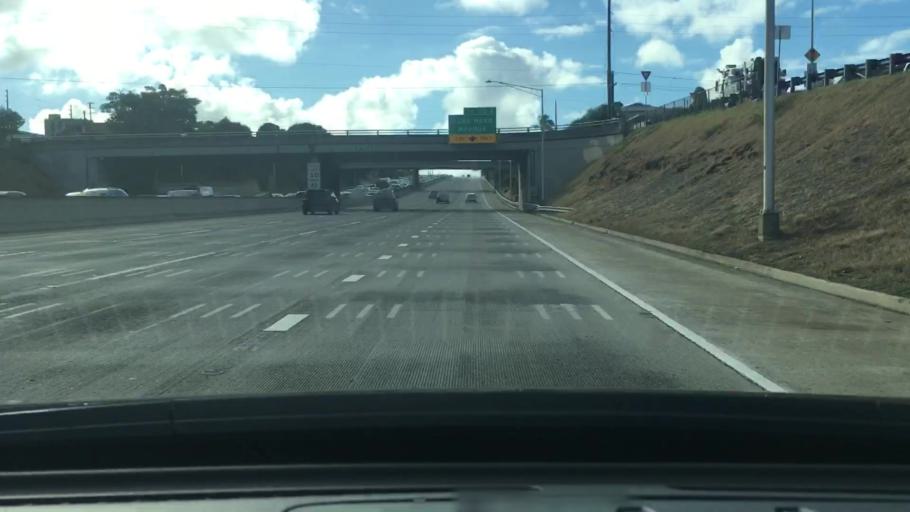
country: US
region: Hawaii
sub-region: Honolulu County
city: Honolulu
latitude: 21.2841
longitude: -157.8079
